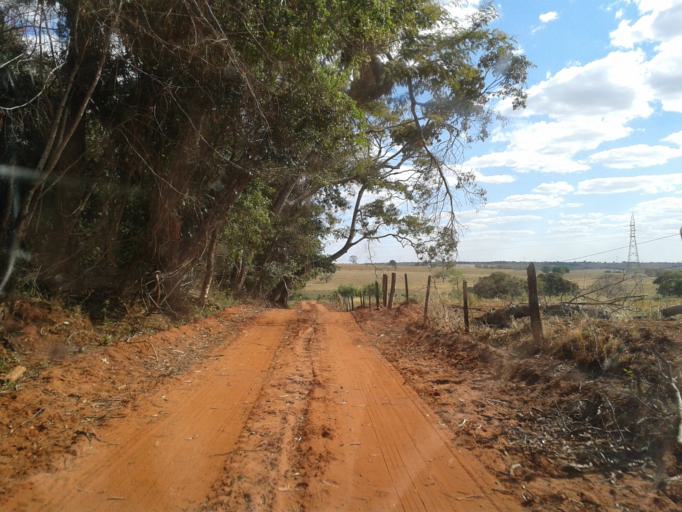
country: BR
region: Minas Gerais
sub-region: Centralina
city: Centralina
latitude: -18.7589
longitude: -49.0826
